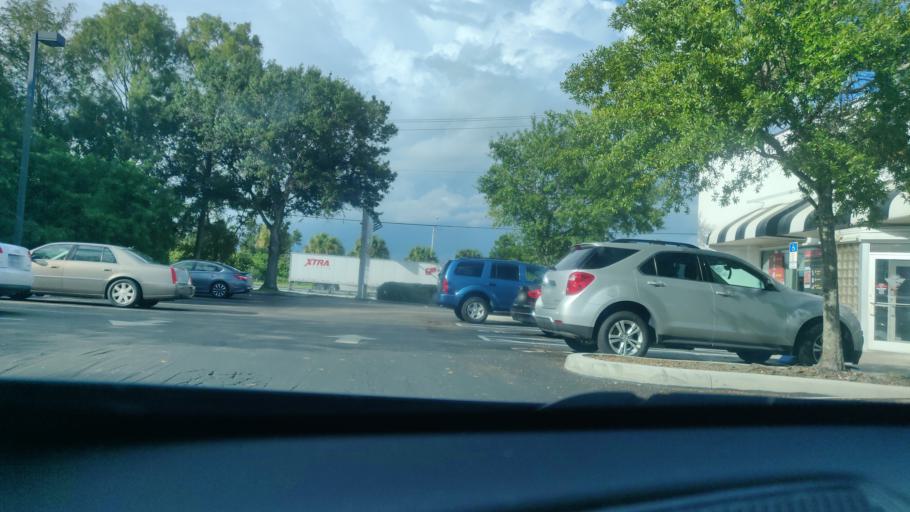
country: US
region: Florida
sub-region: Indian River County
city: West Vero Corridor
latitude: 27.6386
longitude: -80.5215
